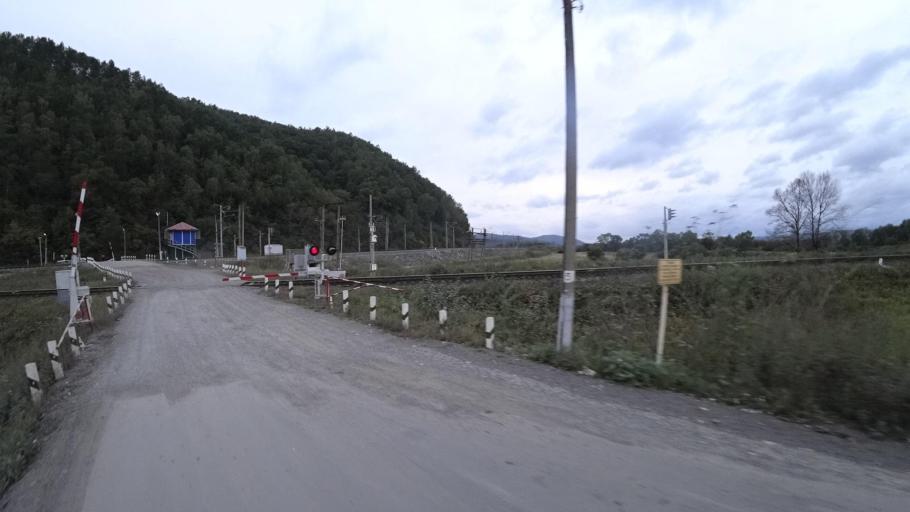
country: RU
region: Jewish Autonomous Oblast
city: Izvestkovyy
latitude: 48.9923
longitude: 131.5378
